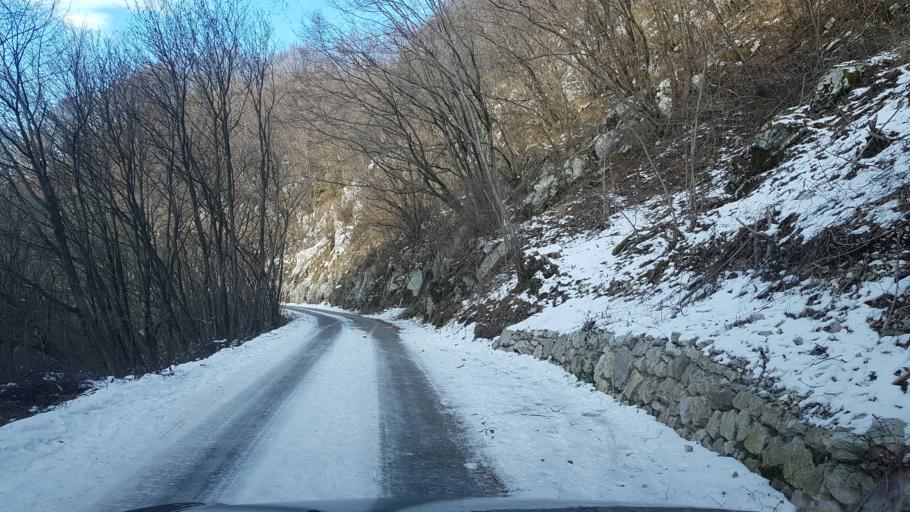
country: IT
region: Friuli Venezia Giulia
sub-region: Provincia di Udine
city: Montenars
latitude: 46.2786
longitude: 13.1582
